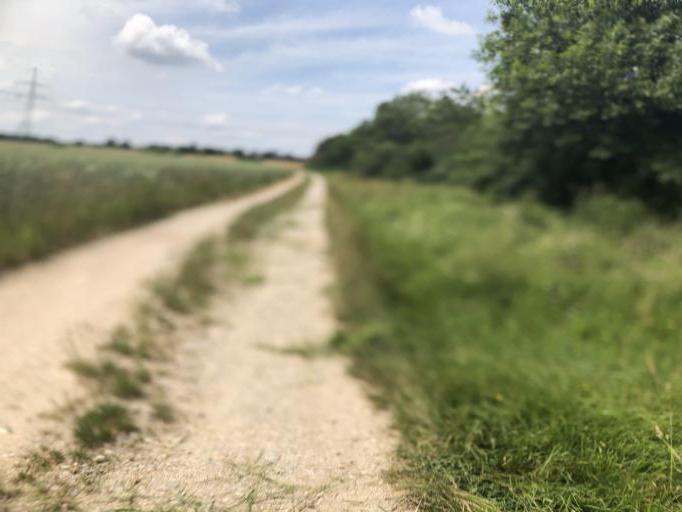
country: DE
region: Bavaria
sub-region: Regierungsbezirk Mittelfranken
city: Erlangen
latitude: 49.5792
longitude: 10.9537
